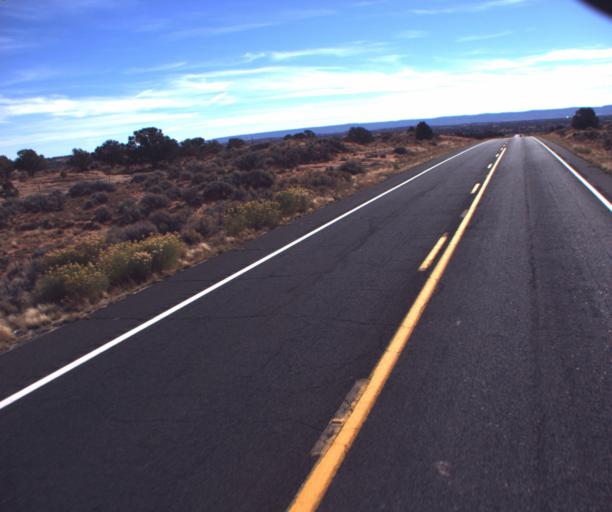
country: US
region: Arizona
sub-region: Coconino County
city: Kaibito
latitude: 36.5668
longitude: -110.7595
